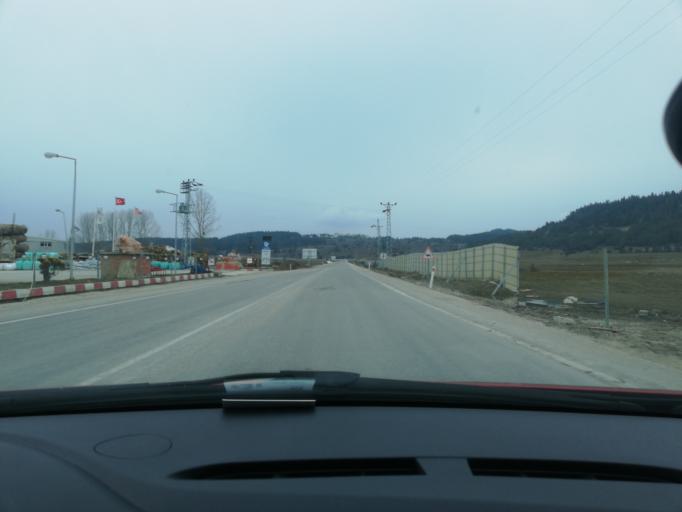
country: TR
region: Kastamonu
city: Agli
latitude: 41.6902
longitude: 33.5545
